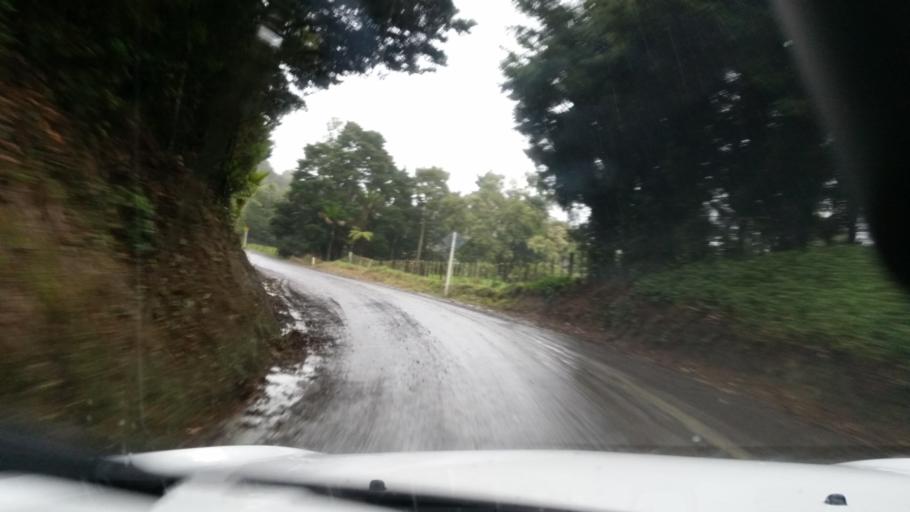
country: NZ
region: Northland
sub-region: Kaipara District
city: Dargaville
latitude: -35.7448
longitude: 173.9633
